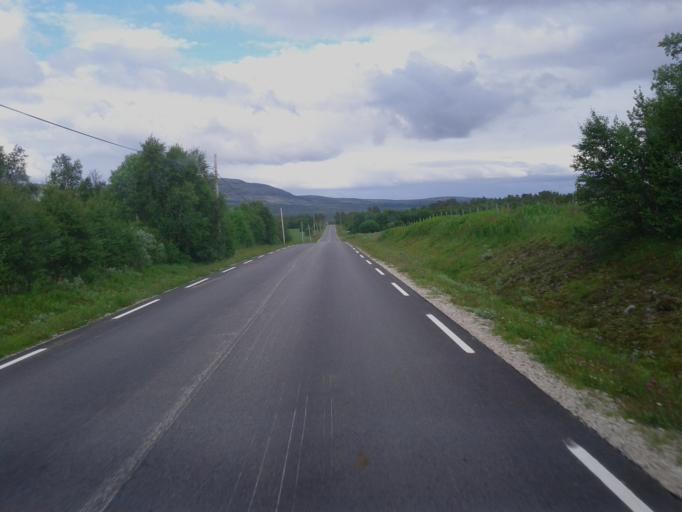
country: NO
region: Sor-Trondelag
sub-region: Roros
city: Roros
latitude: 62.3070
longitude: 11.6929
